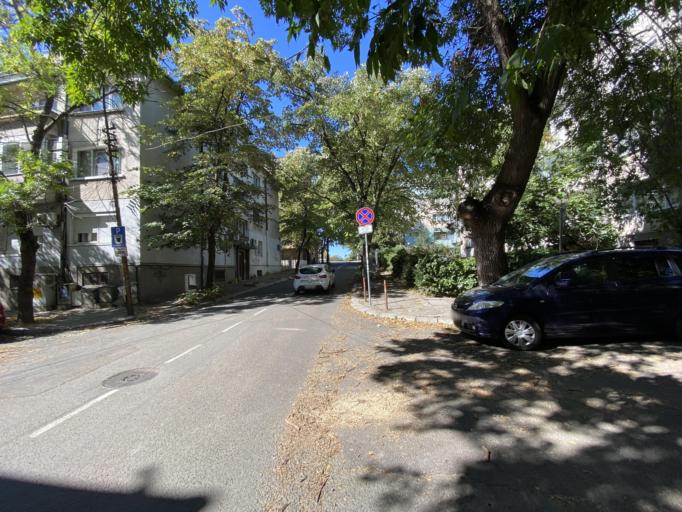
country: BG
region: Burgas
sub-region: Obshtina Burgas
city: Burgas
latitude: 42.4970
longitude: 27.4668
